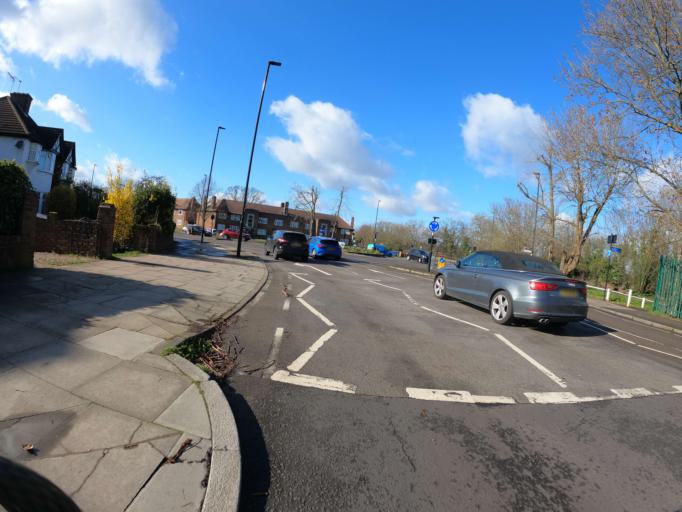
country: GB
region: England
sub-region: Greater London
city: Greenford
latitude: 51.5285
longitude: -0.3269
